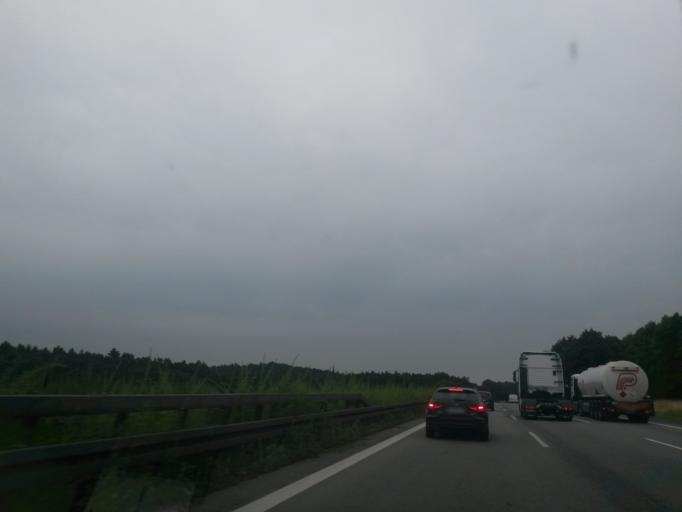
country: DE
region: Bavaria
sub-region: Upper Bavaria
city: Rohrbach
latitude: 48.6367
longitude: 11.5215
